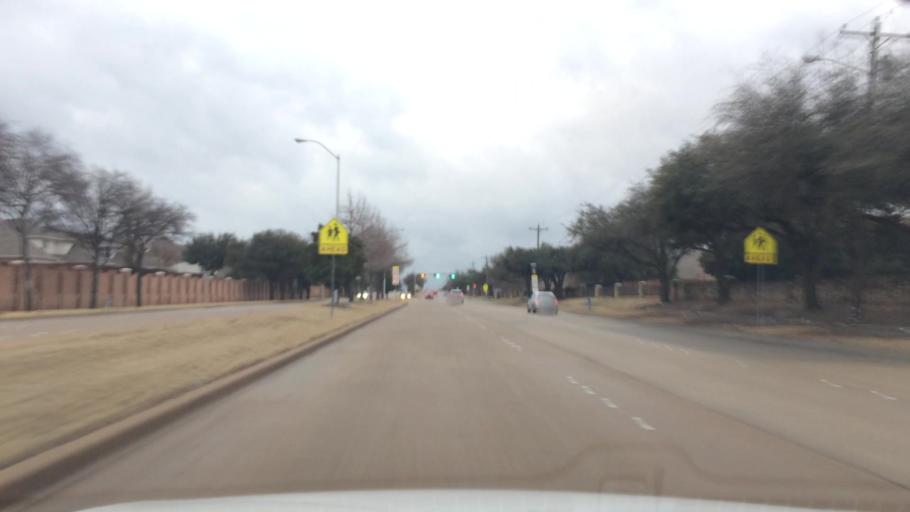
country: US
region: Texas
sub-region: Collin County
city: Frisco
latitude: 33.0950
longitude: -96.7717
